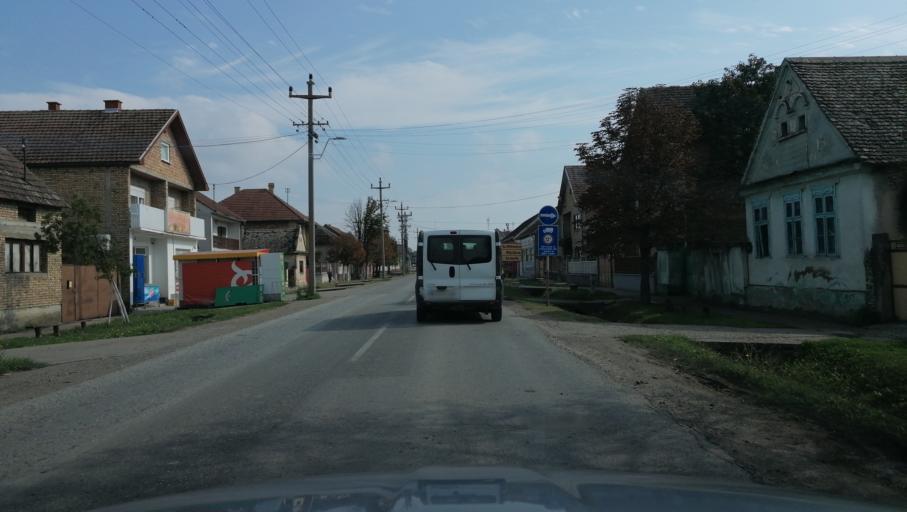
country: RS
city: Ravnje
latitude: 45.0236
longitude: 19.4015
